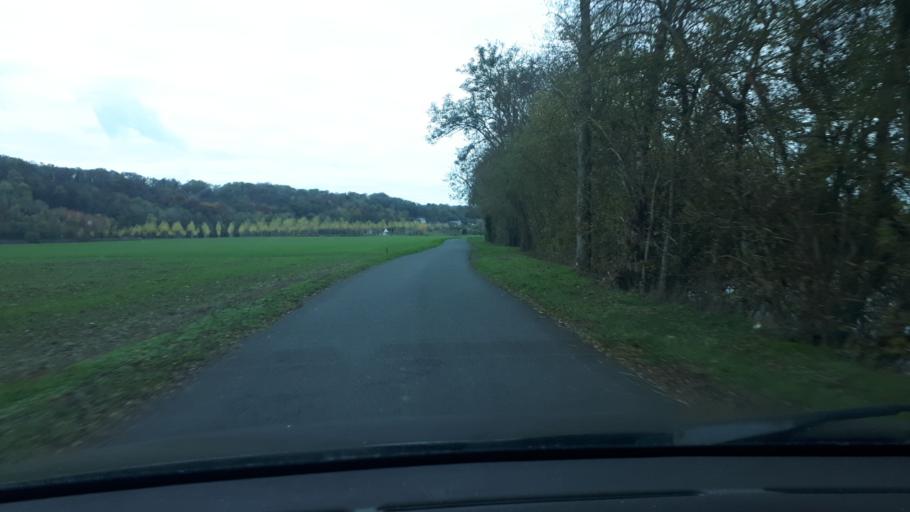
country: FR
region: Centre
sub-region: Departement du Loir-et-Cher
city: Lunay
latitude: 47.7681
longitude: 0.9438
